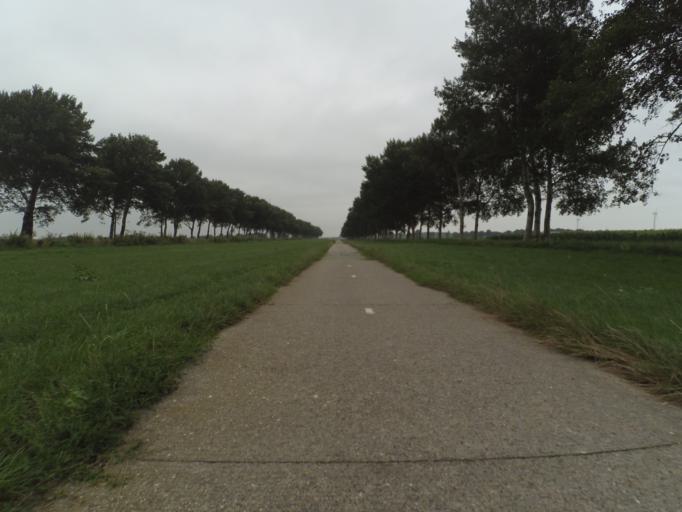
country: NL
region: Flevoland
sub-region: Gemeente Zeewolde
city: Zeewolde
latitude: 52.3979
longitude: 5.4622
